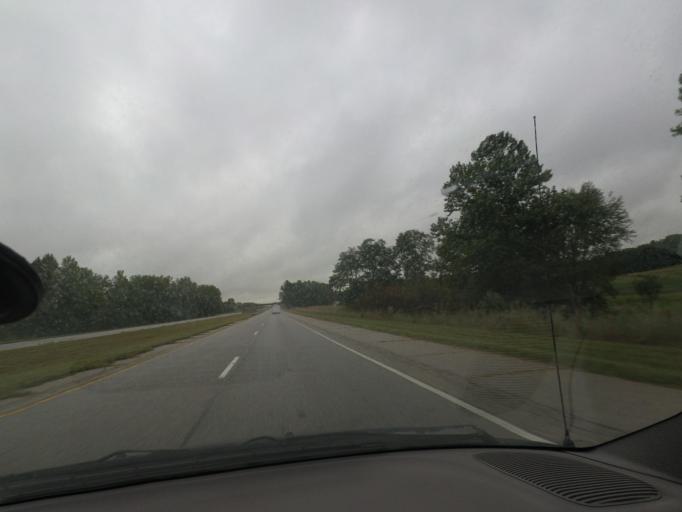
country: US
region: Illinois
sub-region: Adams County
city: Payson
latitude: 39.7281
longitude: -91.1619
